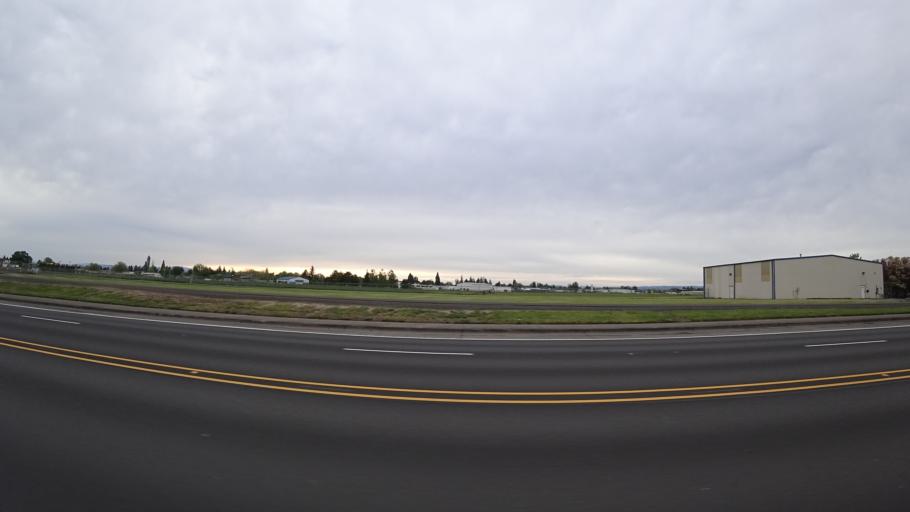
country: US
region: Oregon
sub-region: Washington County
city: Hillsboro
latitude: 45.5316
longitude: -122.9519
